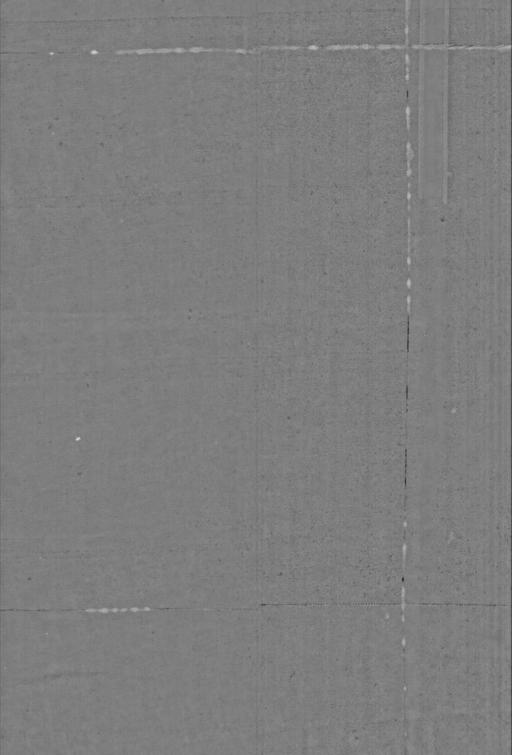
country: US
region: Maryland
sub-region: Prince George's County
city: Colmar Manor
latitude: 38.9178
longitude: -76.9538
